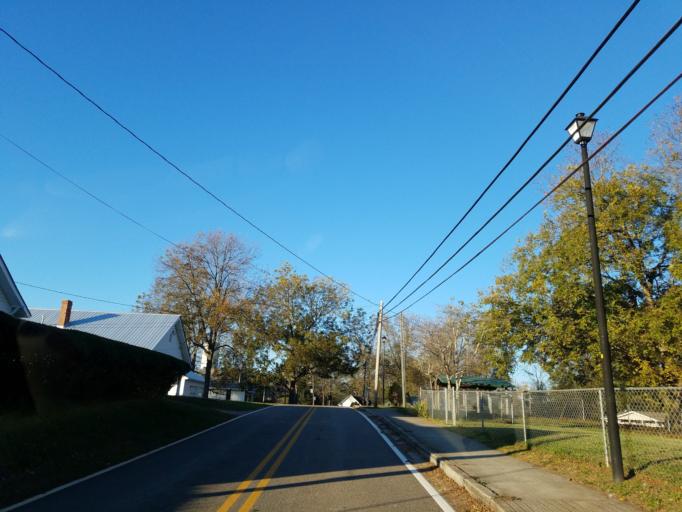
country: US
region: Georgia
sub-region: Pickens County
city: Nelson
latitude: 34.3790
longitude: -84.3656
